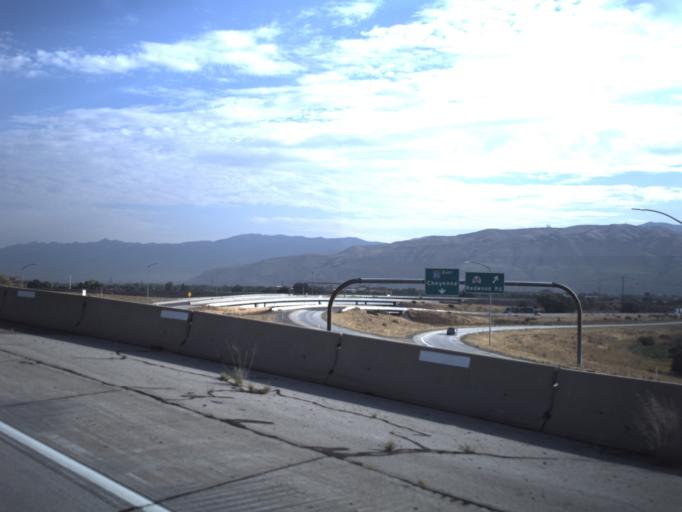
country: US
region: Utah
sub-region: Salt Lake County
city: Salt Lake City
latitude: 40.7625
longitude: -111.9499
